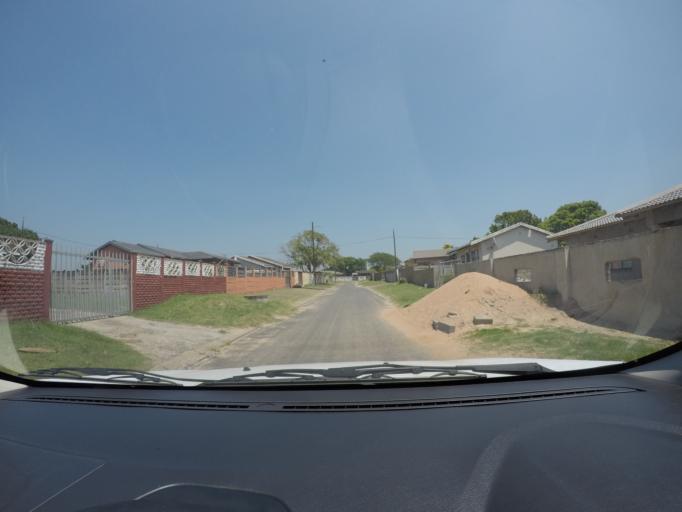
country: ZA
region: KwaZulu-Natal
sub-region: uThungulu District Municipality
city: eSikhawini
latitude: -28.8694
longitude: 31.9188
